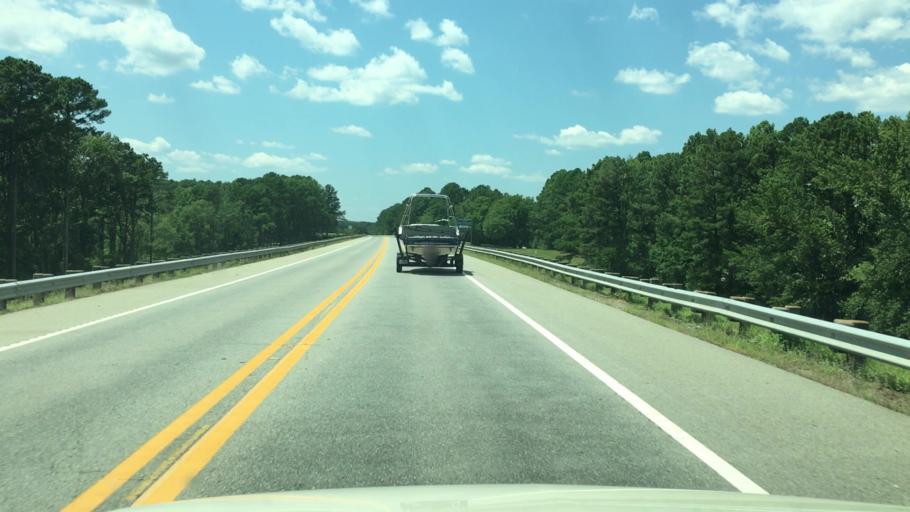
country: US
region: Arkansas
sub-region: Clark County
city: Arkadelphia
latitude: 34.2467
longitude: -93.1113
